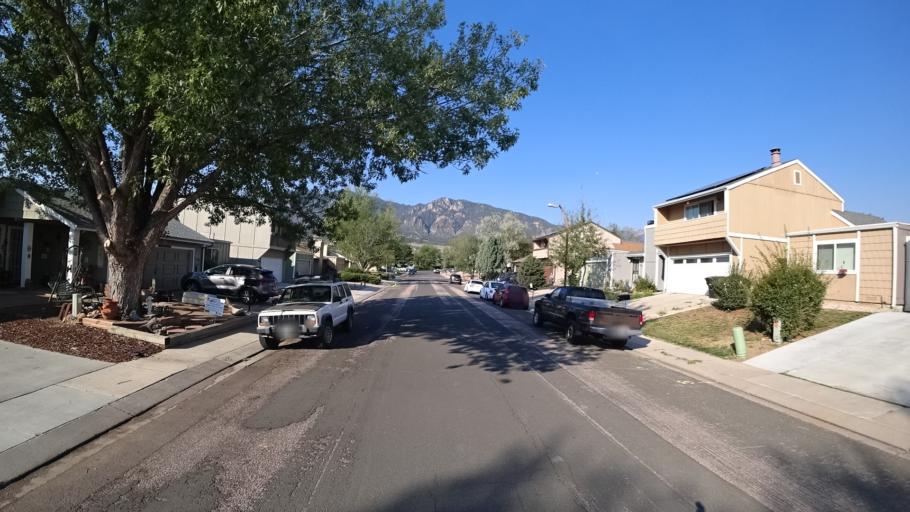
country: US
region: Colorado
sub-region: El Paso County
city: Stratmoor
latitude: 38.7784
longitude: -104.8132
